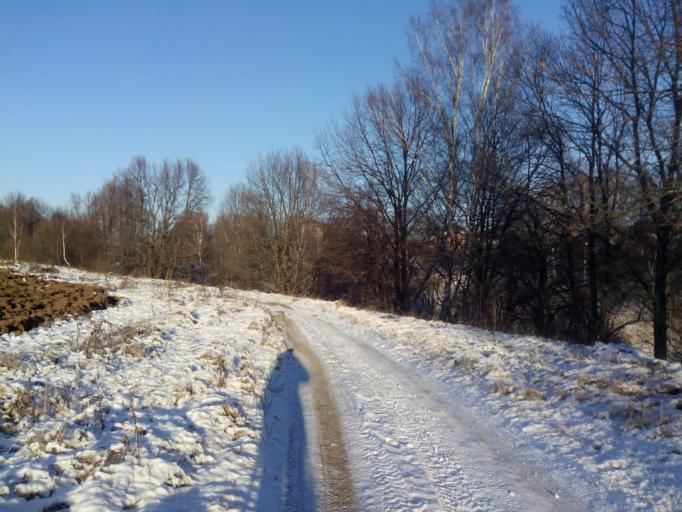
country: RU
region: Moskovskaya
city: Yakovlevskoye
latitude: 55.4939
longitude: 37.9533
